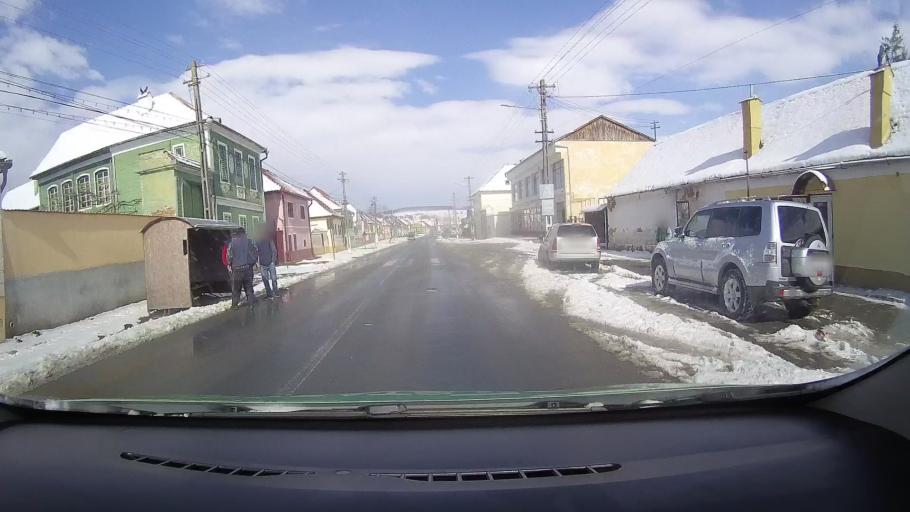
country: RO
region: Sibiu
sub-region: Comuna Altina
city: Altina
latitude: 45.9277
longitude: 24.4622
